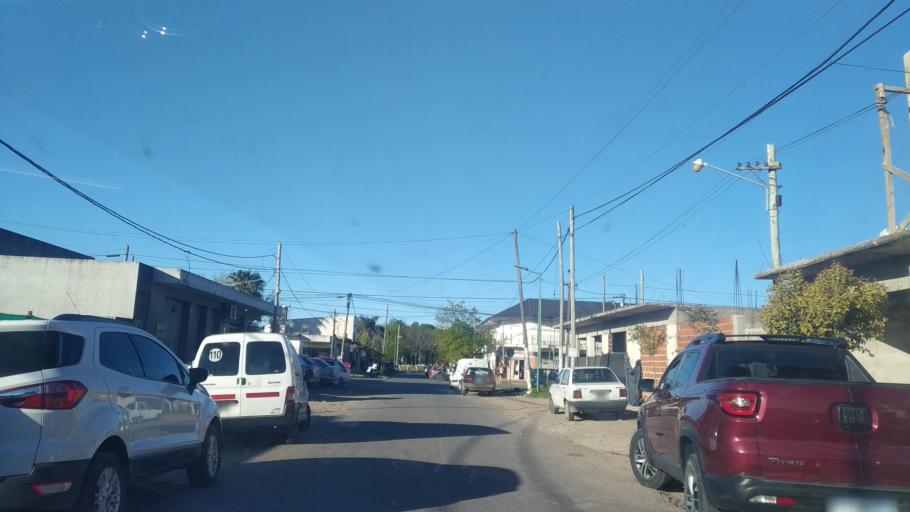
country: AR
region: Buenos Aires
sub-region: Partido de La Plata
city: La Plata
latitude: -34.9966
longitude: -58.0476
